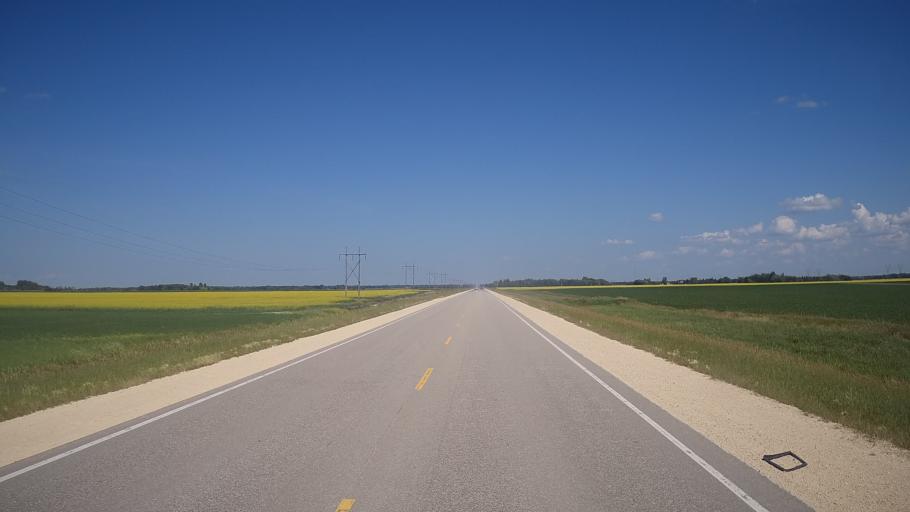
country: CA
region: Manitoba
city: Stonewall
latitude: 50.1227
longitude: -97.4096
